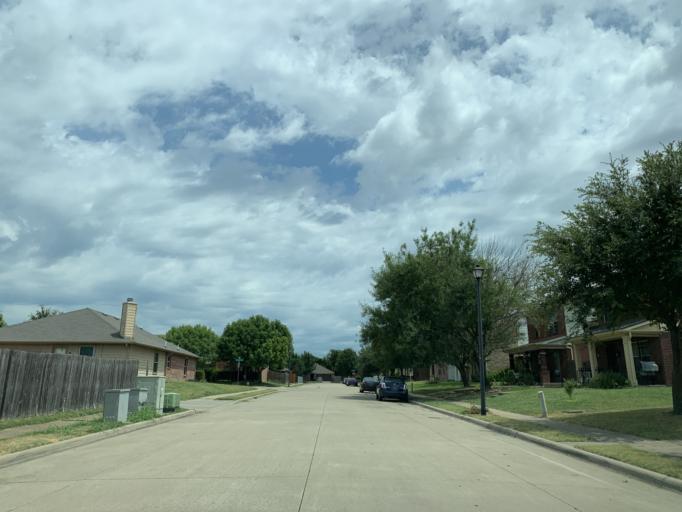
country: US
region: Texas
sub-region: Dallas County
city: DeSoto
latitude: 32.6552
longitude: -96.8122
